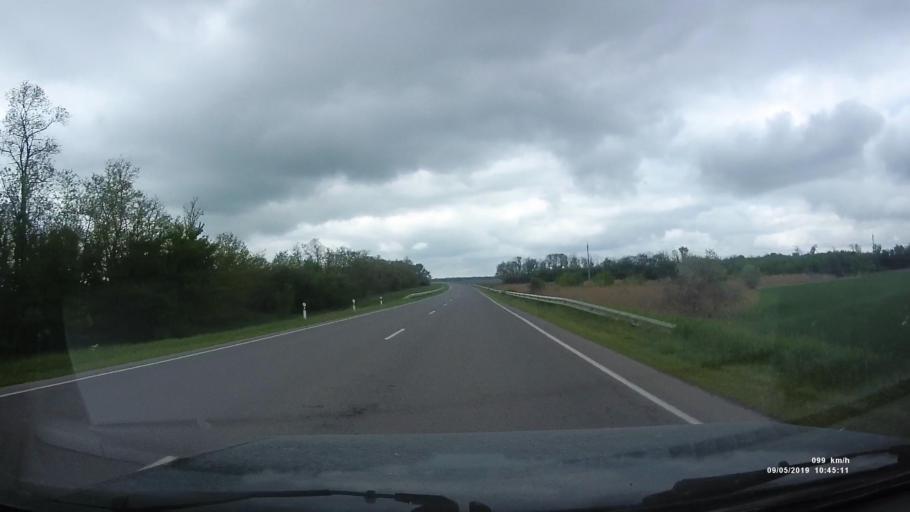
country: RU
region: Rostov
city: Peshkovo
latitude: 46.9974
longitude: 39.3731
